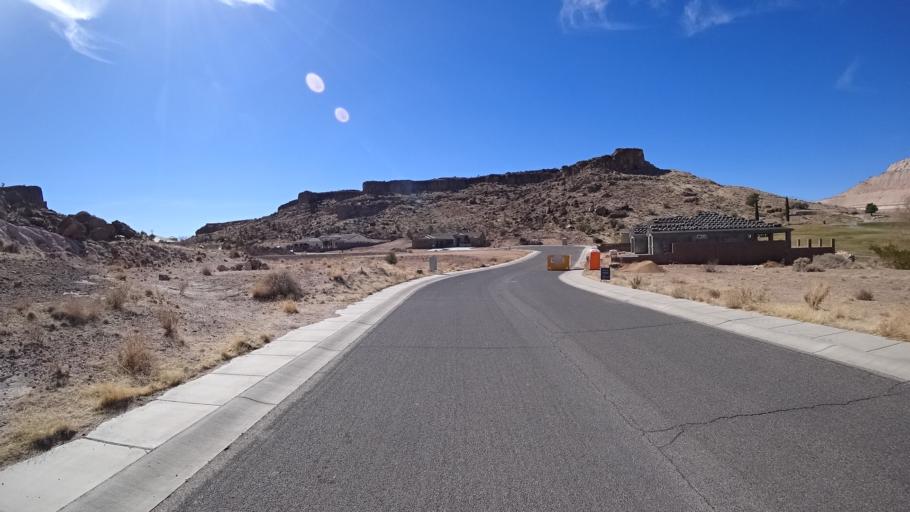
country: US
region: Arizona
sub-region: Mohave County
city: Kingman
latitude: 35.2092
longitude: -114.0547
